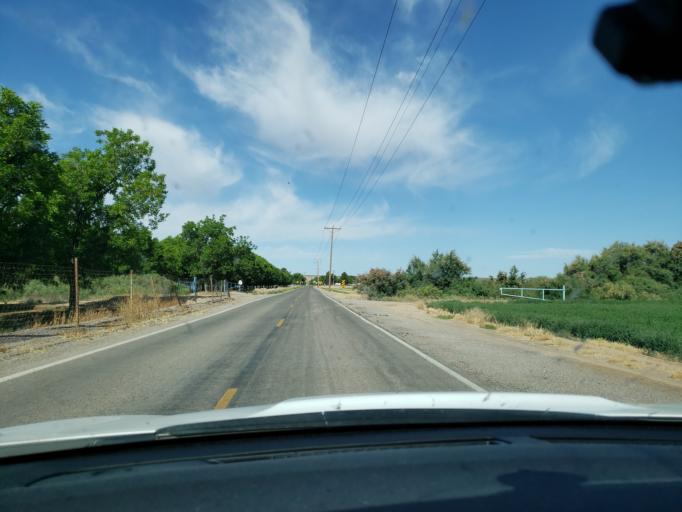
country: US
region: New Mexico
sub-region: Dona Ana County
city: Vado
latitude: 32.0626
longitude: -106.6732
